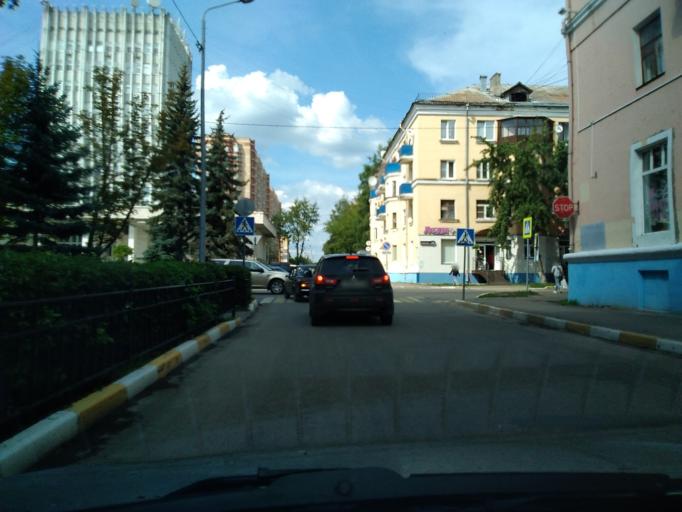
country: RU
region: Moskovskaya
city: Voskresensk
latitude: 55.3231
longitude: 38.6738
